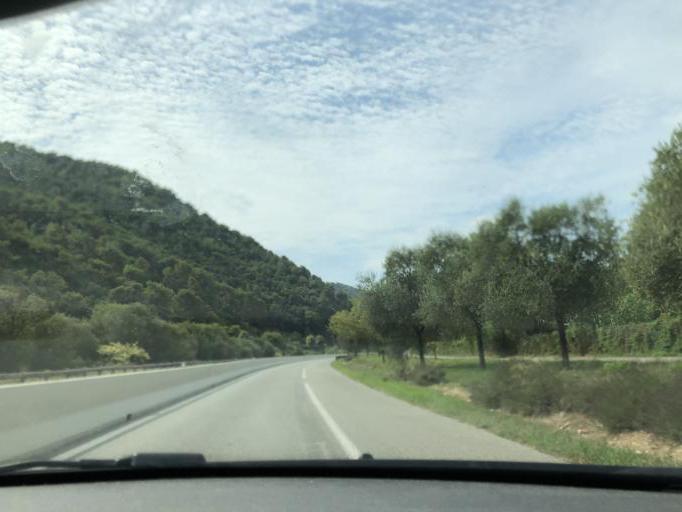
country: FR
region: Provence-Alpes-Cote d'Azur
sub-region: Departement des Alpes-Maritimes
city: Cantaron
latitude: 43.7769
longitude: 7.3369
